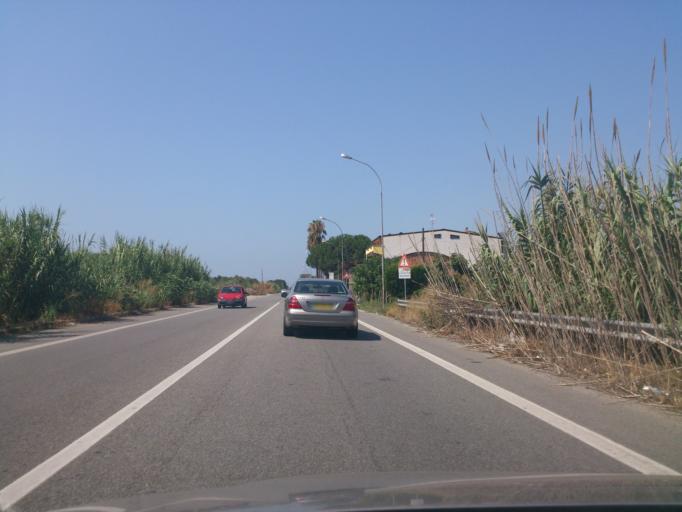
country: IT
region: Calabria
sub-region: Provincia di Reggio Calabria
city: Caulonia Marina
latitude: 38.3525
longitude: 16.4793
